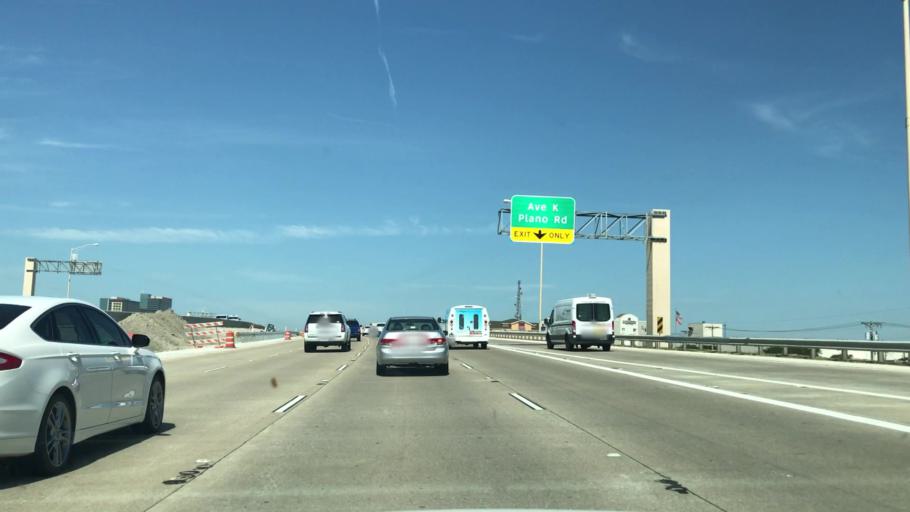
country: US
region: Texas
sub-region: Collin County
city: Plano
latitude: 33.0025
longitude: -96.6801
